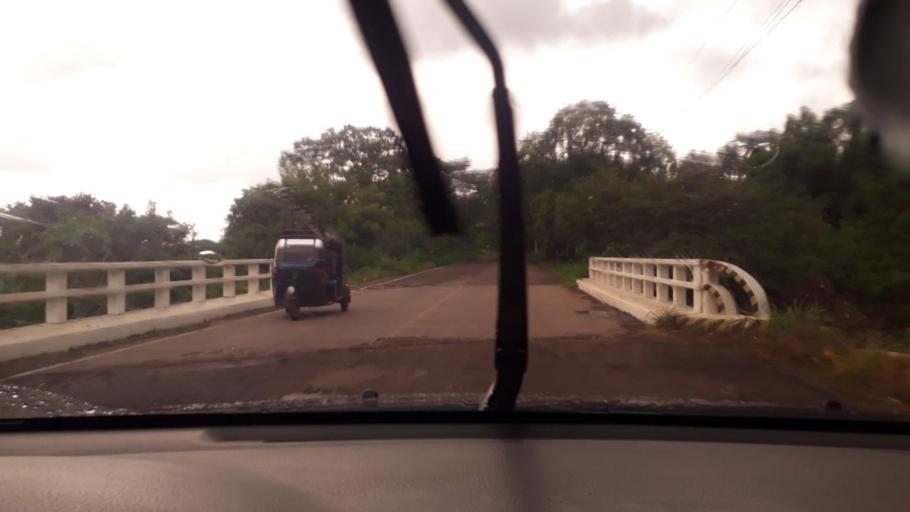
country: GT
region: Jutiapa
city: Comapa
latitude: 14.1073
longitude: -89.9657
